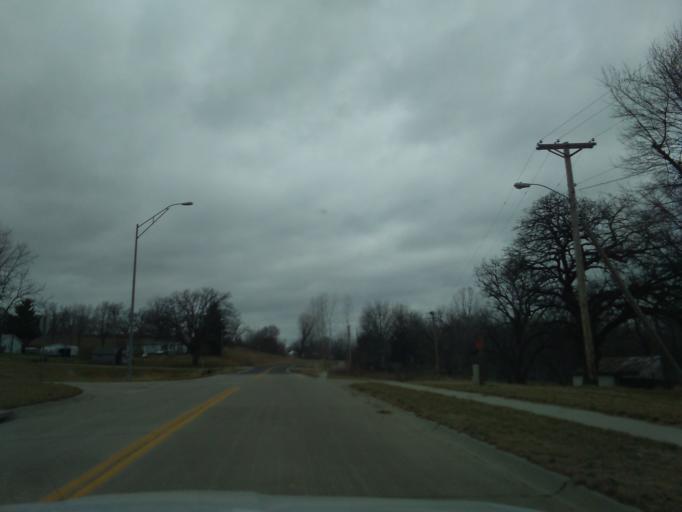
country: US
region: Nebraska
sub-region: Richardson County
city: Falls City
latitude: 40.0526
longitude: -95.4301
